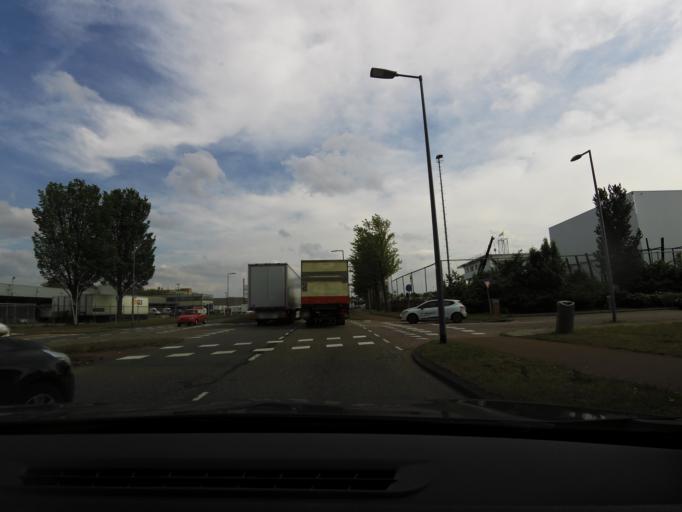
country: NL
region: South Holland
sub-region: Gemeente Schiedam
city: Schiedam
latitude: 51.9262
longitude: 4.4167
